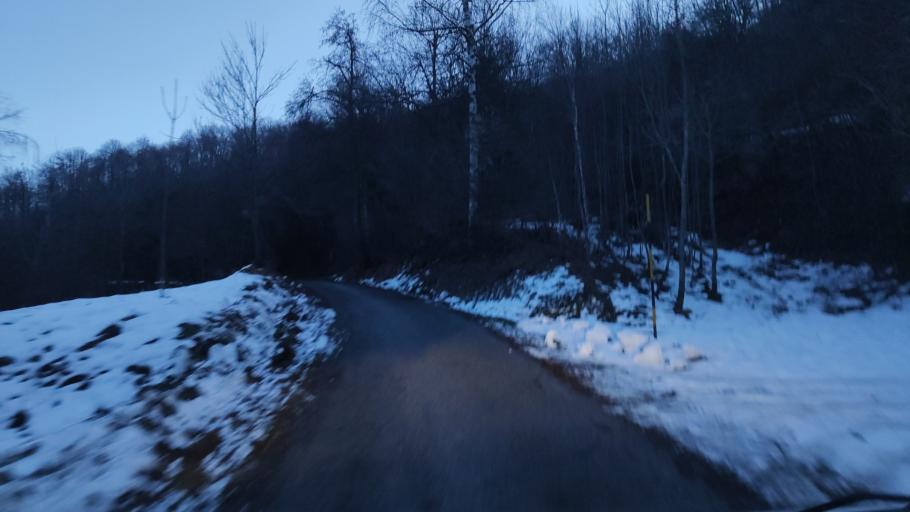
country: IT
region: Piedmont
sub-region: Provincia di Cuneo
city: Viola
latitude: 44.2819
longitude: 7.9606
